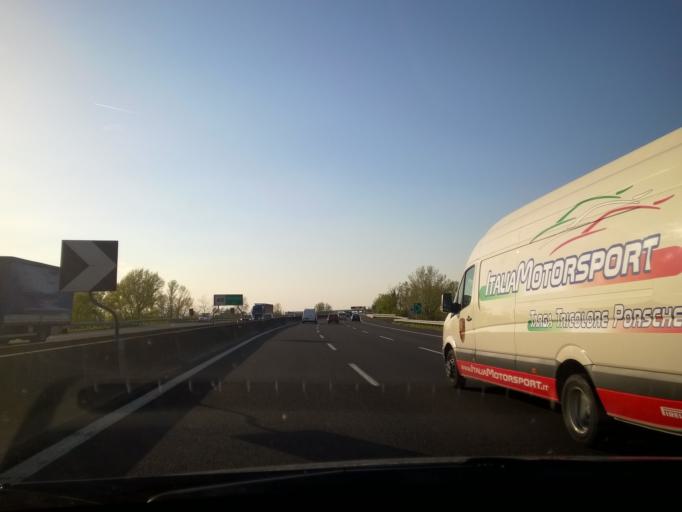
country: IT
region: Emilia-Romagna
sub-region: Provincia di Bologna
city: Toscanella
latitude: 44.4170
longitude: 11.6260
